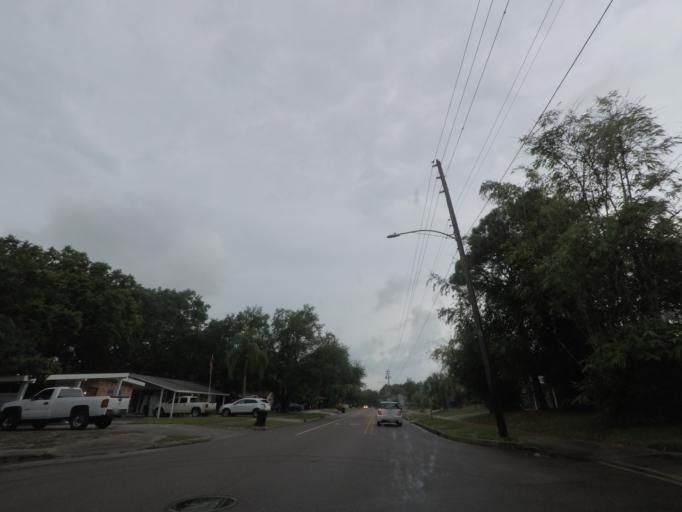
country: US
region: Florida
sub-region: Pinellas County
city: Treasure Island
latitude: 27.7923
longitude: -82.7497
